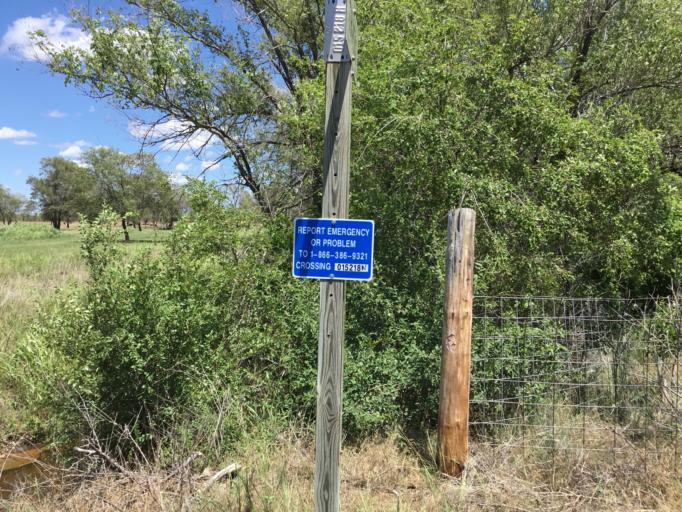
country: US
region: Kansas
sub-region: Sedgwick County
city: Cheney
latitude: 37.6089
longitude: -97.9300
